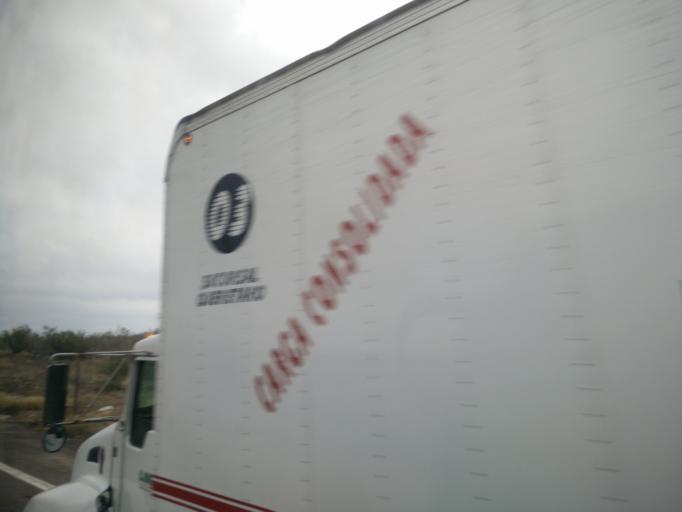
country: MX
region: Sonora
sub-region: Hermosillo
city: Miguel Aleman (La Doce)
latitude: 28.5117
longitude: -111.0456
